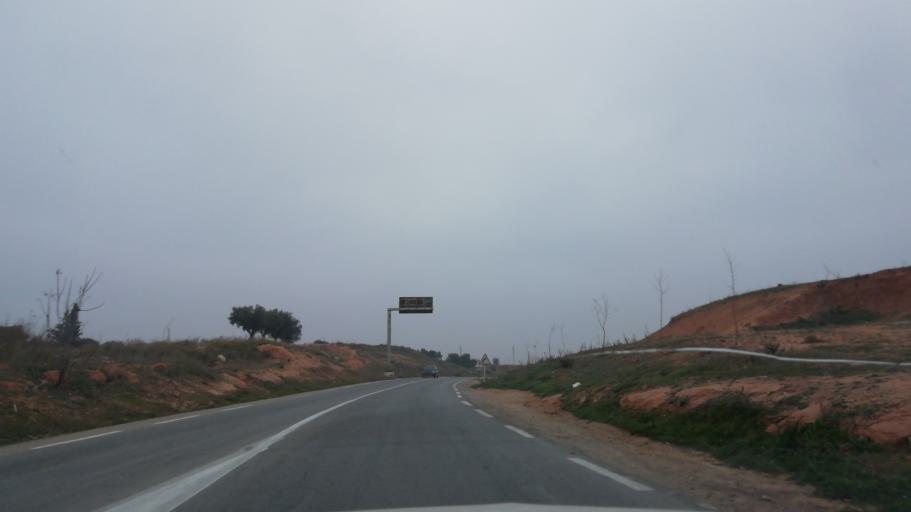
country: DZ
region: Mascara
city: Mascara
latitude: 35.4142
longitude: 0.1460
